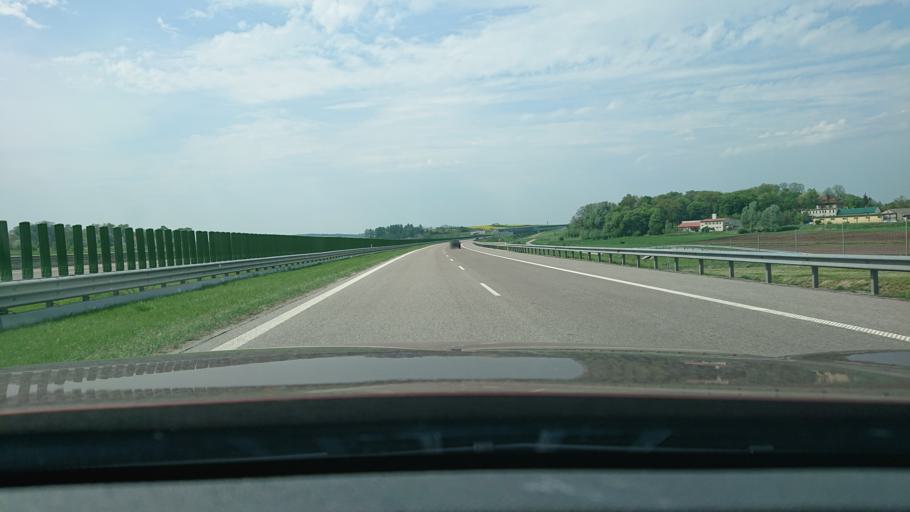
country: PL
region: Subcarpathian Voivodeship
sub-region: Powiat jaroslawski
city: Rokietnica
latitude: 49.9389
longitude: 22.6779
